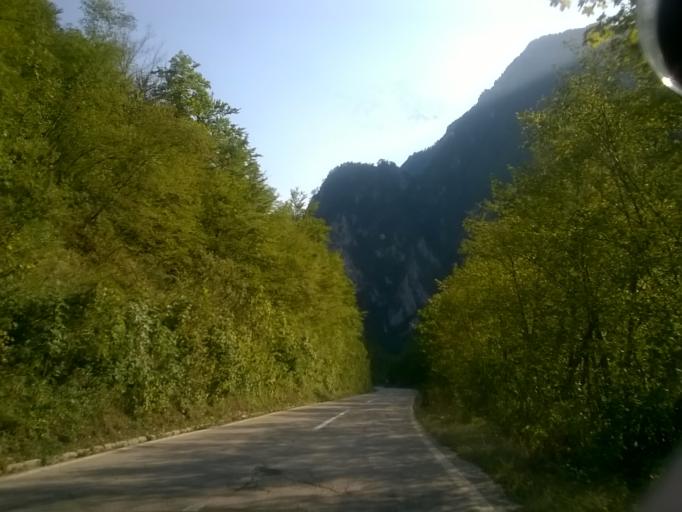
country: ME
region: Opstina Pluzine
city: Pluzine
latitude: 43.3082
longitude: 18.8520
